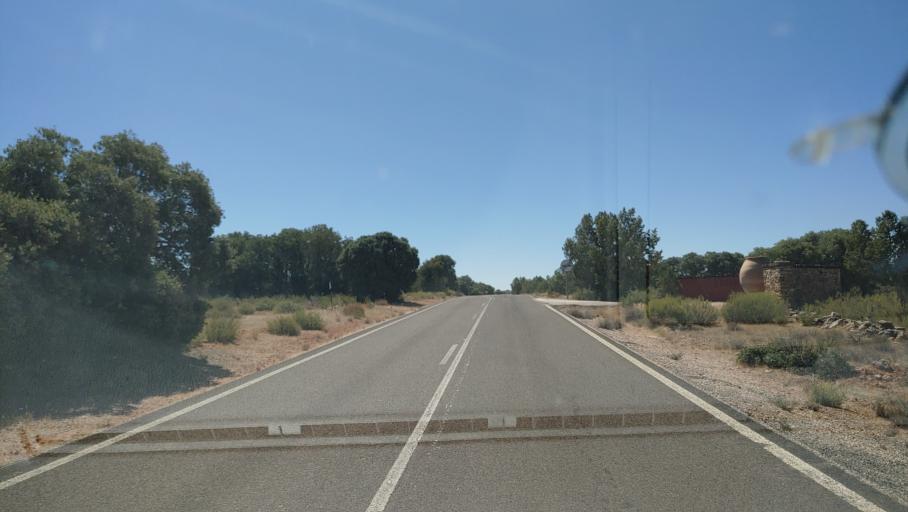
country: ES
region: Castille-La Mancha
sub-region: Provincia de Albacete
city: Ossa de Montiel
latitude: 38.8827
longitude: -2.7760
